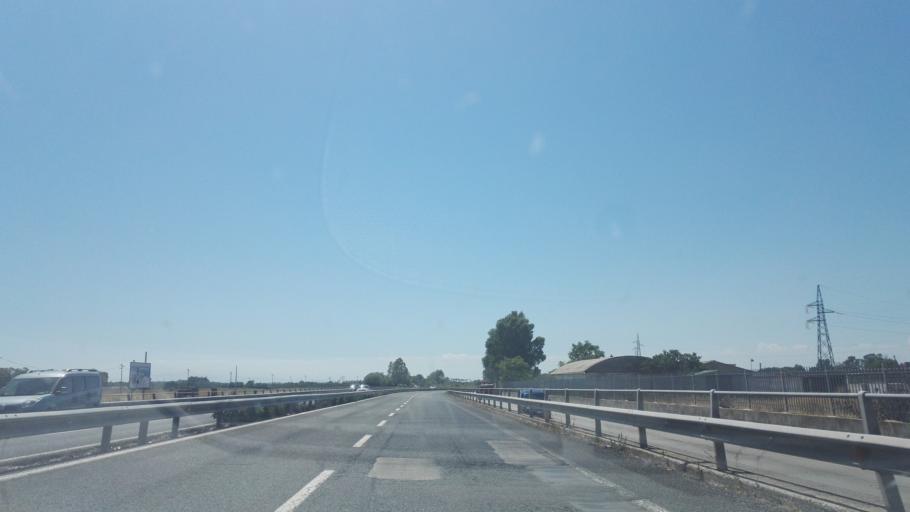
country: IT
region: Apulia
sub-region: Provincia di Taranto
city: Marina di Ginosa
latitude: 40.4985
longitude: 16.9559
